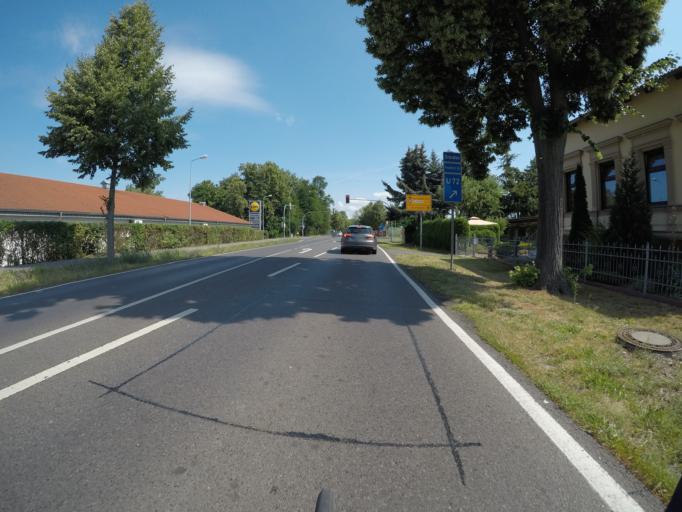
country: DE
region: Brandenburg
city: Bernau bei Berlin
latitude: 52.6689
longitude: 13.5824
